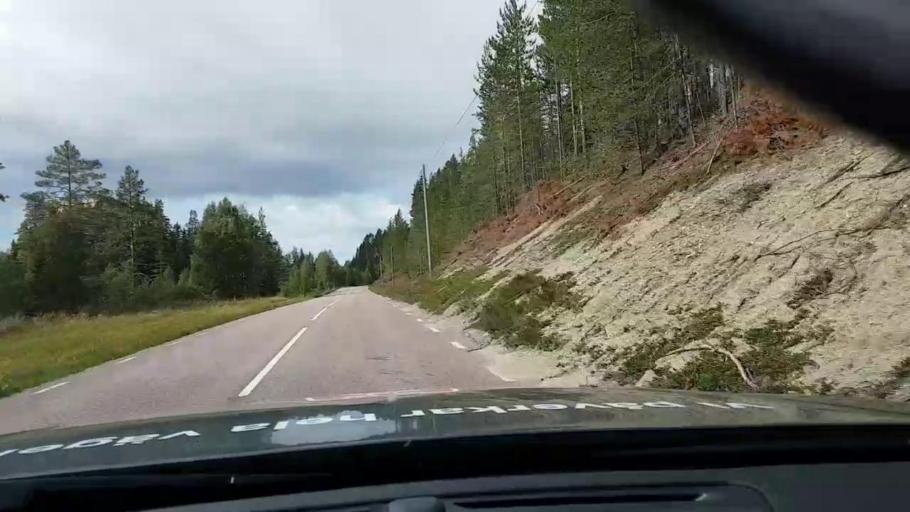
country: SE
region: Vaesterbotten
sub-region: Asele Kommun
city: Asele
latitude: 63.8635
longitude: 17.3691
